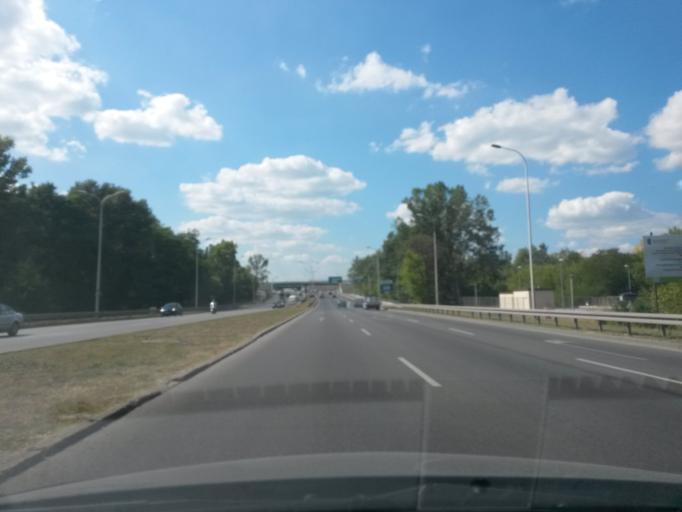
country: PL
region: Masovian Voivodeship
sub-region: Warszawa
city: Bielany
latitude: 52.3010
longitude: 20.9517
